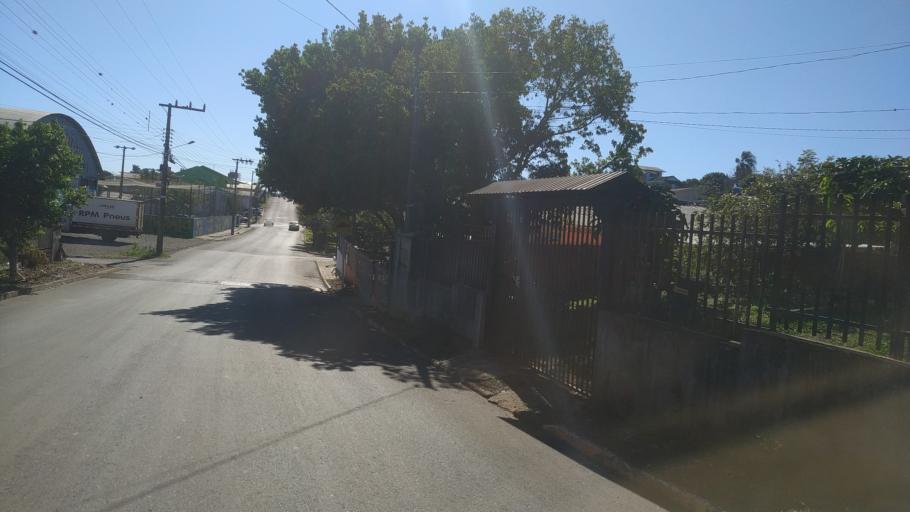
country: BR
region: Santa Catarina
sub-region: Chapeco
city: Chapeco
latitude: -27.1177
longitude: -52.6241
